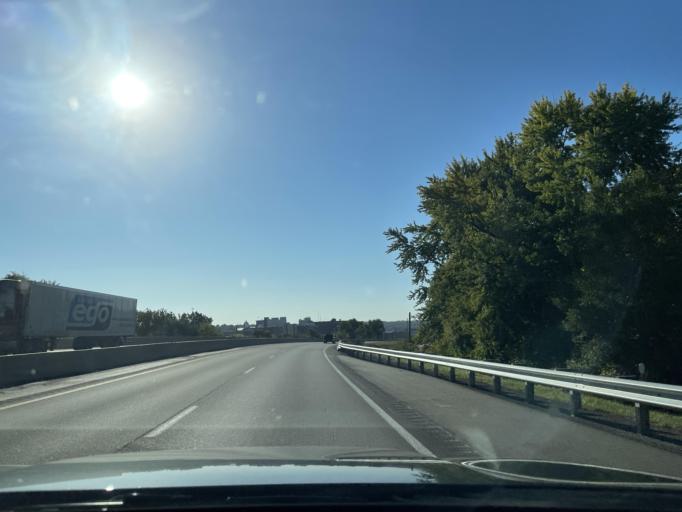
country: US
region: Missouri
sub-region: Buchanan County
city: Saint Joseph
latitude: 39.7752
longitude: -94.8630
